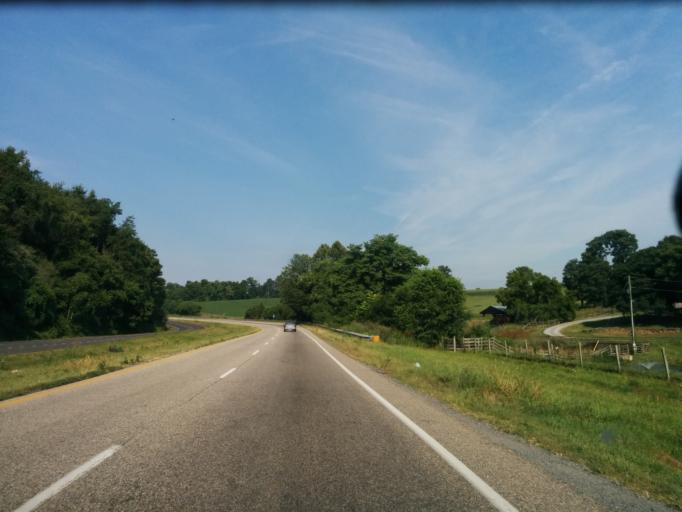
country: US
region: Virginia
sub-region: Rockbridge County
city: East Lexington
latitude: 37.7583
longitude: -79.4003
